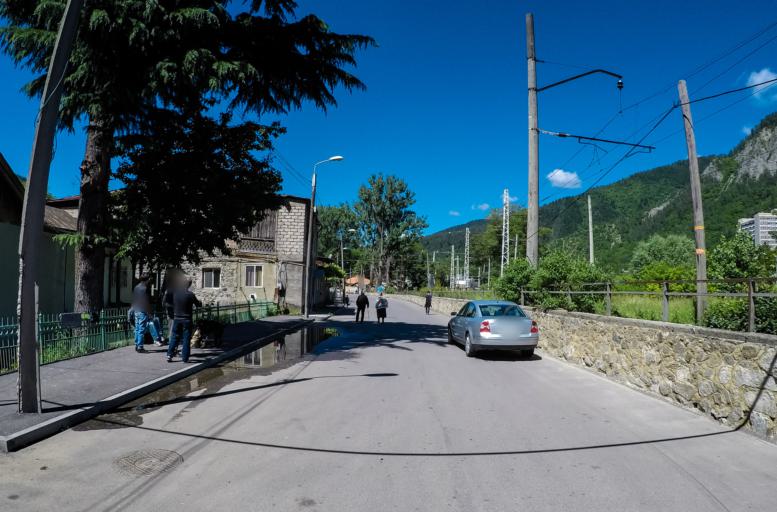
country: GE
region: Samtskhe-Javakheti
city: Borjomi
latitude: 41.8416
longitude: 43.3888
